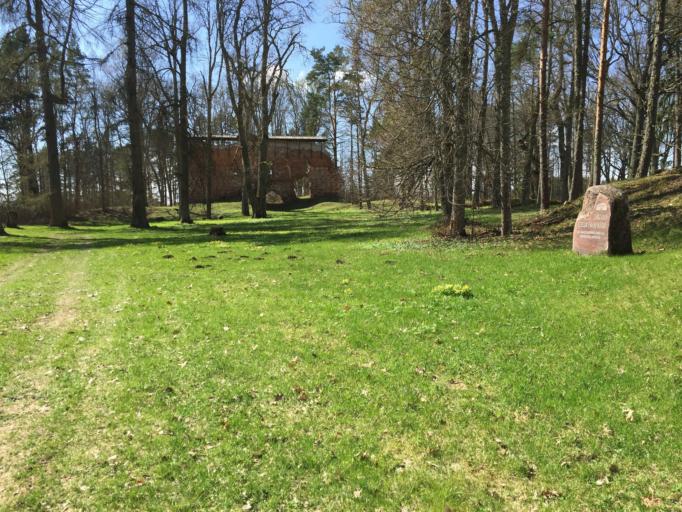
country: EE
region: Tartu
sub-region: Elva linn
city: Elva
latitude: 58.1544
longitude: 26.2286
